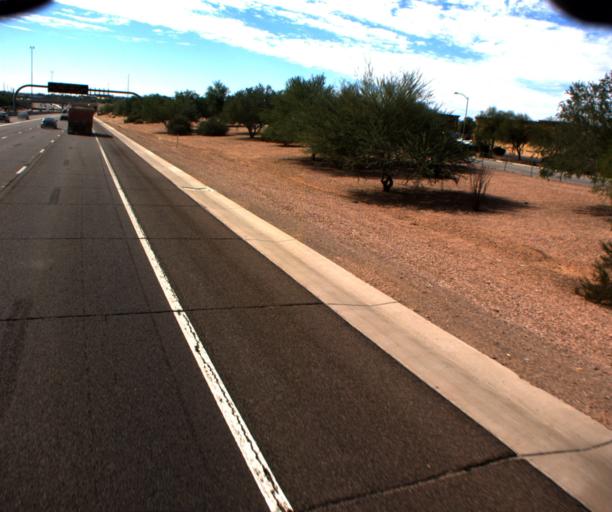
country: US
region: Arizona
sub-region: Maricopa County
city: Paradise Valley
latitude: 33.6242
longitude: -111.8908
